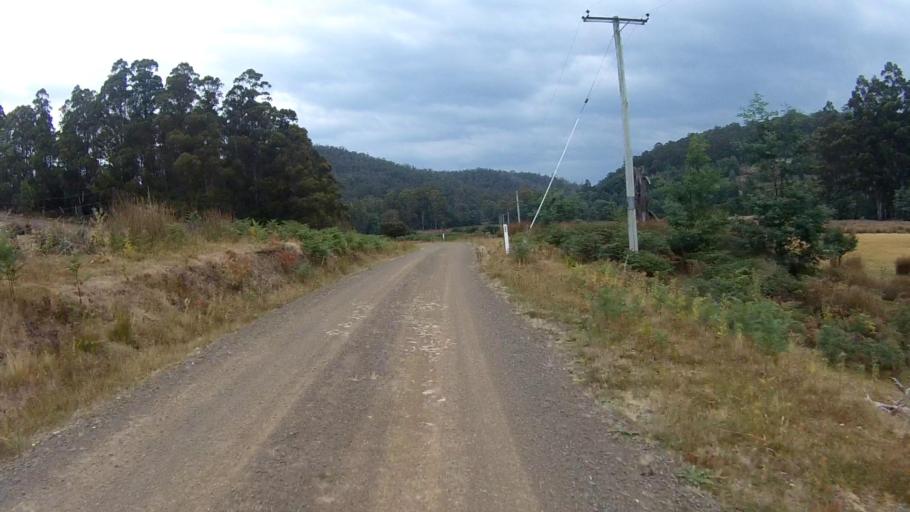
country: AU
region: Tasmania
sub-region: Kingborough
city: Kettering
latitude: -43.2177
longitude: 147.1766
